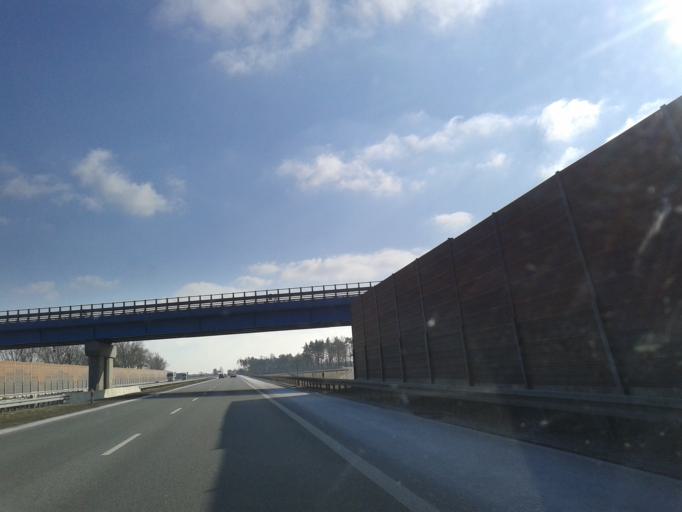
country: PL
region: Kujawsko-Pomorskie
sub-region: Powiat aleksandrowski
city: Raciazek
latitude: 52.8091
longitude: 18.8144
